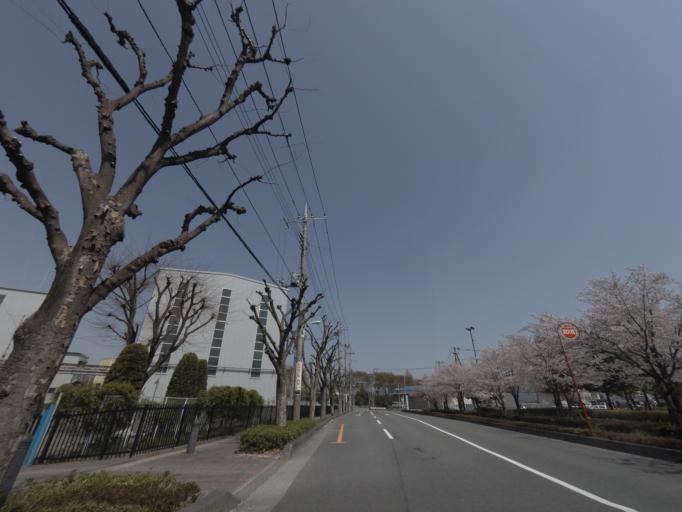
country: JP
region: Saitama
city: Shiki
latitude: 35.8605
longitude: 139.6037
